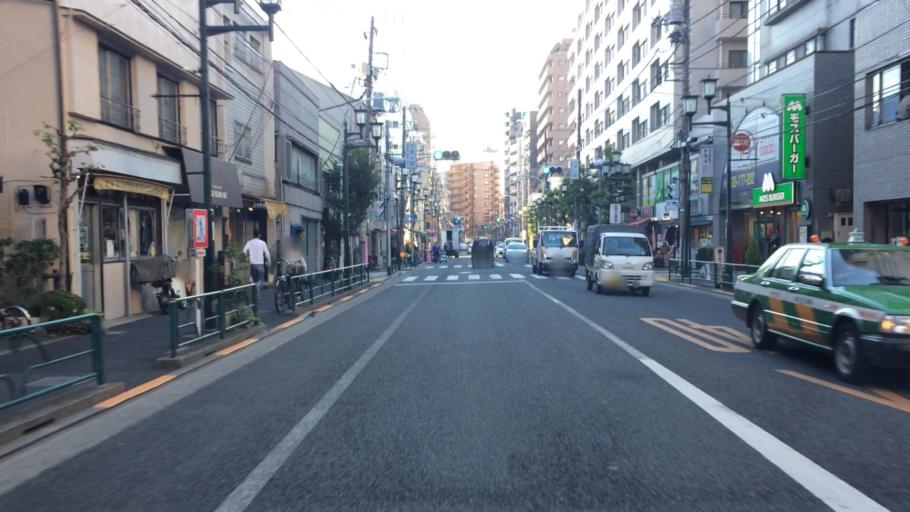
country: JP
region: Tokyo
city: Tokyo
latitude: 35.7239
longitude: 139.7628
